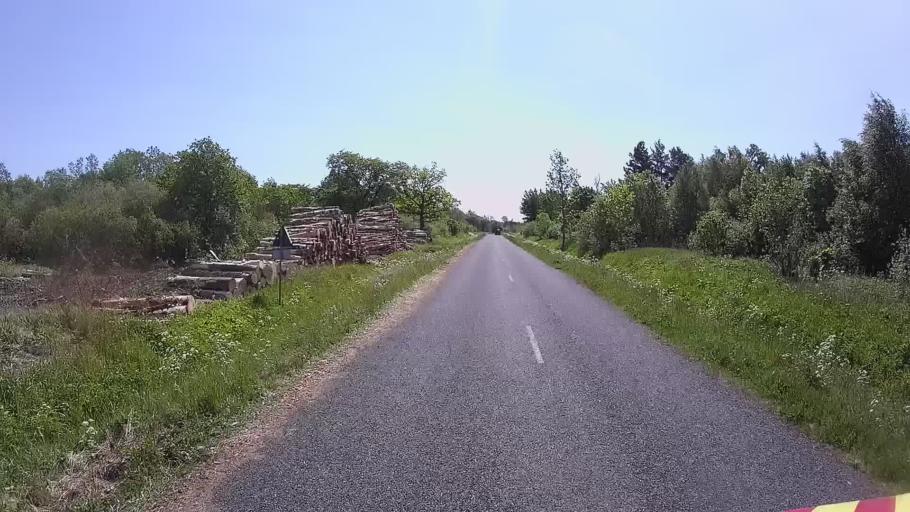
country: LV
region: Dundaga
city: Dundaga
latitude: 57.9394
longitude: 22.0901
